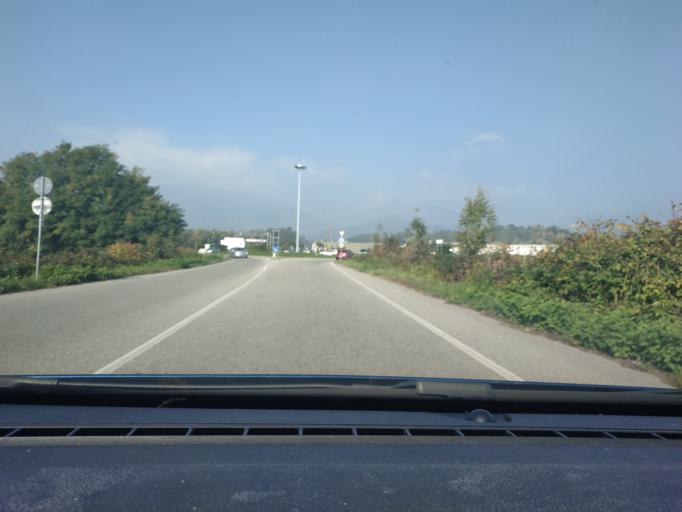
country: IT
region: Piedmont
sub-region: Provincia di Biella
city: Occhieppo Inferiore
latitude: 45.5490
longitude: 8.0339
